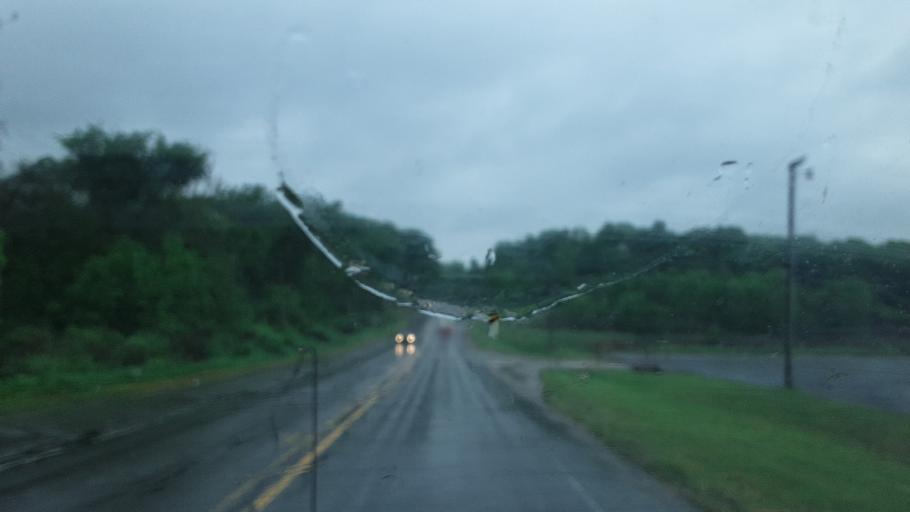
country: US
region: Indiana
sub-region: Steuben County
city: Fremont
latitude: 41.7461
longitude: -85.0005
